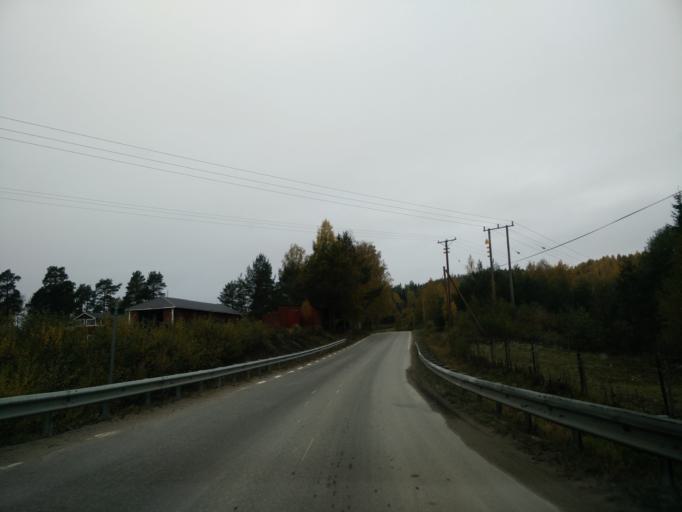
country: SE
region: Vaesternorrland
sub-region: Sundsvalls Kommun
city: Nolby
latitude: 62.2944
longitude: 17.3458
